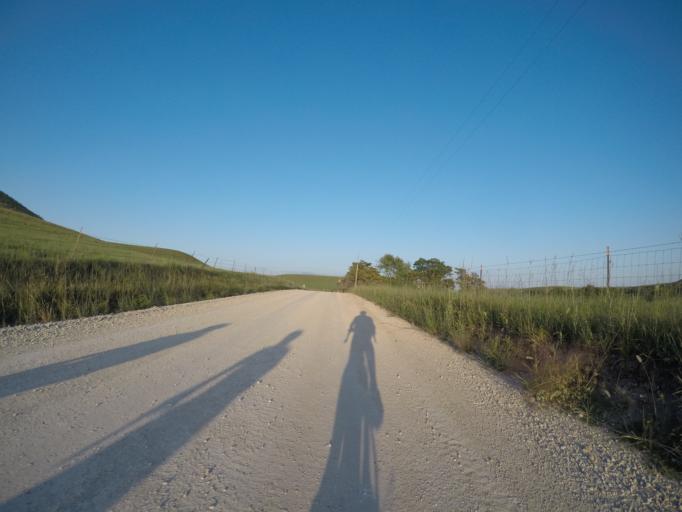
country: US
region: Kansas
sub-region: Riley County
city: Ogden
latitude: 39.0151
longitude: -96.6700
